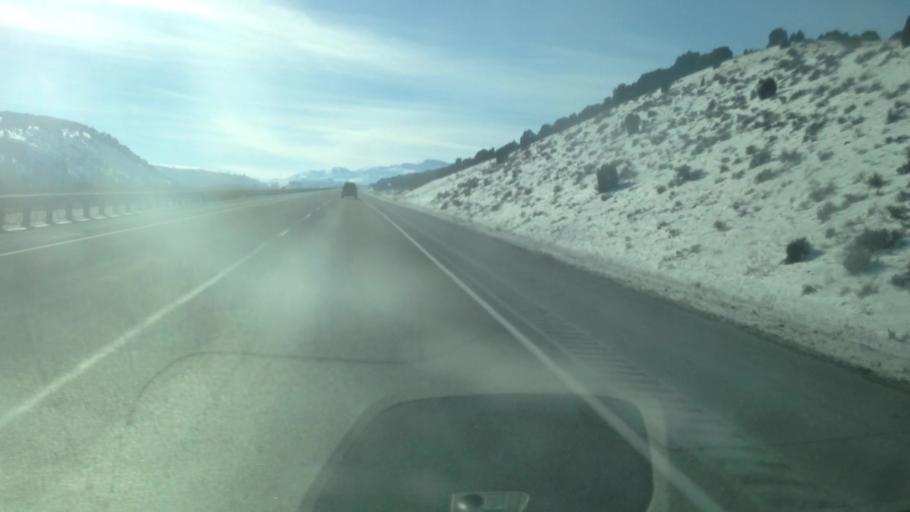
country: US
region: Idaho
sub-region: Oneida County
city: Malad City
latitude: 42.3652
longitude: -112.2148
